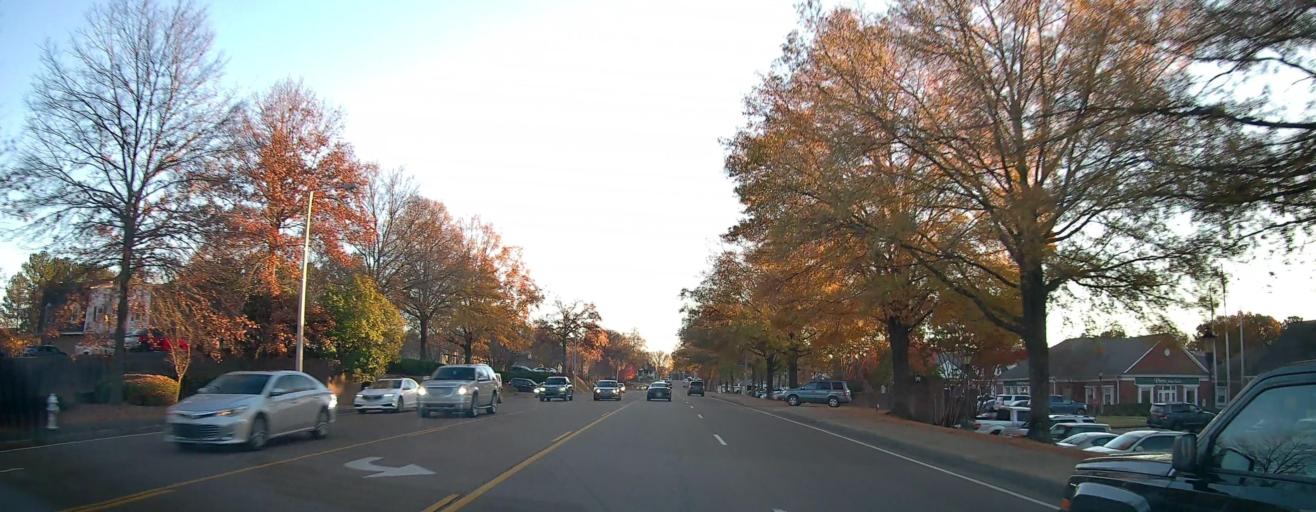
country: US
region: Tennessee
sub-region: Shelby County
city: Germantown
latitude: 35.0917
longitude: -89.8116
